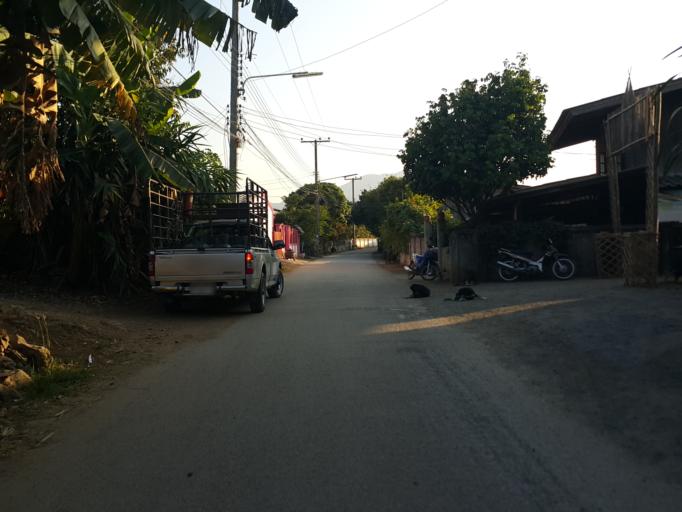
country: TH
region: Chiang Mai
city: Mae On
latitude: 18.7739
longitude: 99.2572
